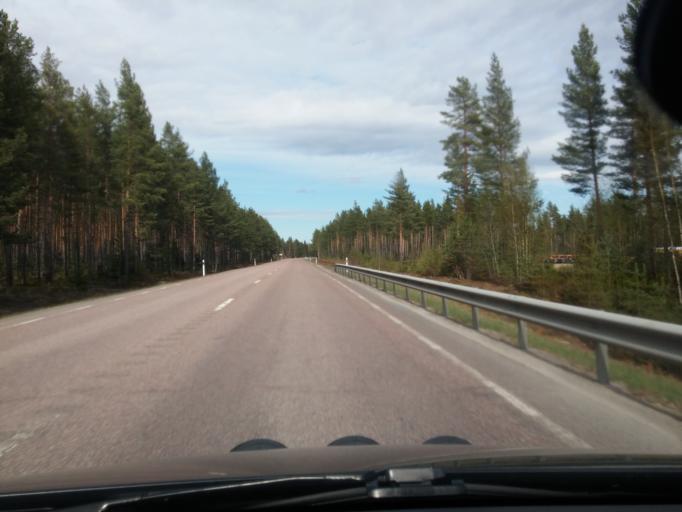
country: SE
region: Gaevleborg
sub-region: Ljusdals Kommun
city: Farila
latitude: 61.8032
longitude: 15.9022
